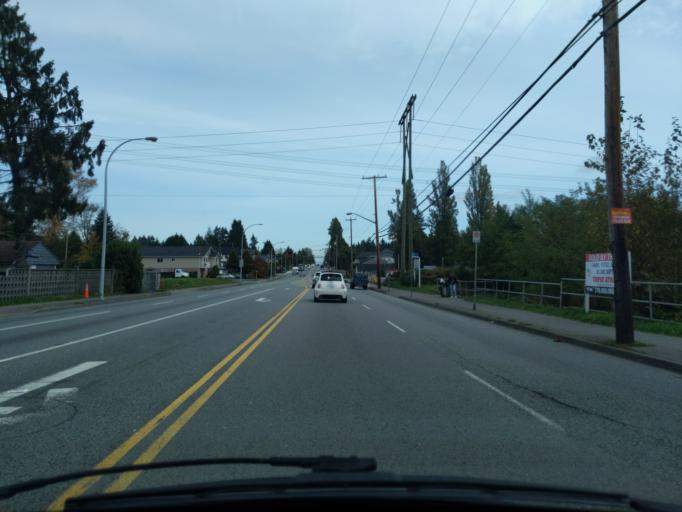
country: CA
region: British Columbia
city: New Westminster
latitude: 49.1988
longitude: -122.8340
